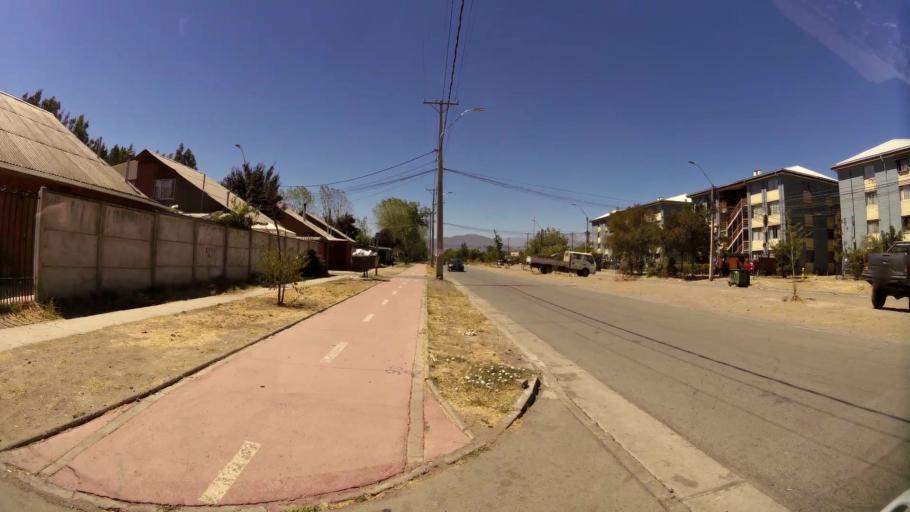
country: CL
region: O'Higgins
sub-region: Provincia de Cachapoal
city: Rancagua
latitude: -34.1485
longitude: -70.7239
